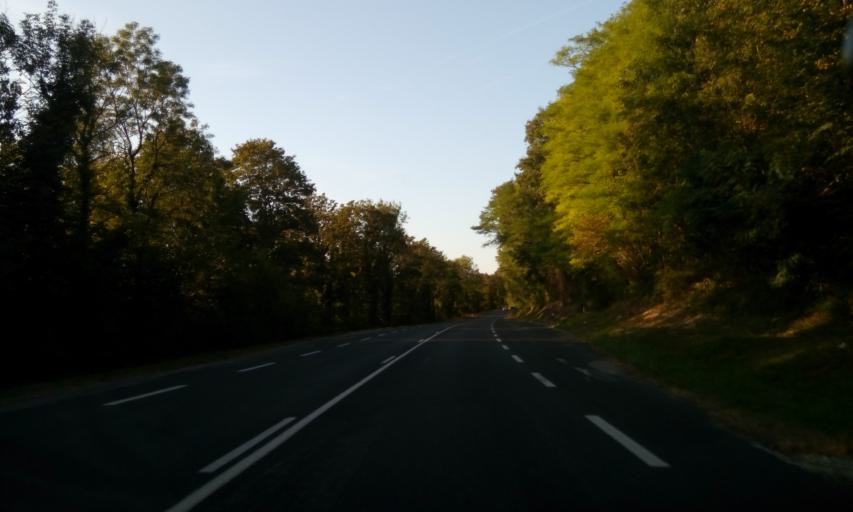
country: FR
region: Rhone-Alpes
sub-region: Departement de l'Ain
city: Neuville-sur-Ain
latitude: 46.0679
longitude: 5.3840
